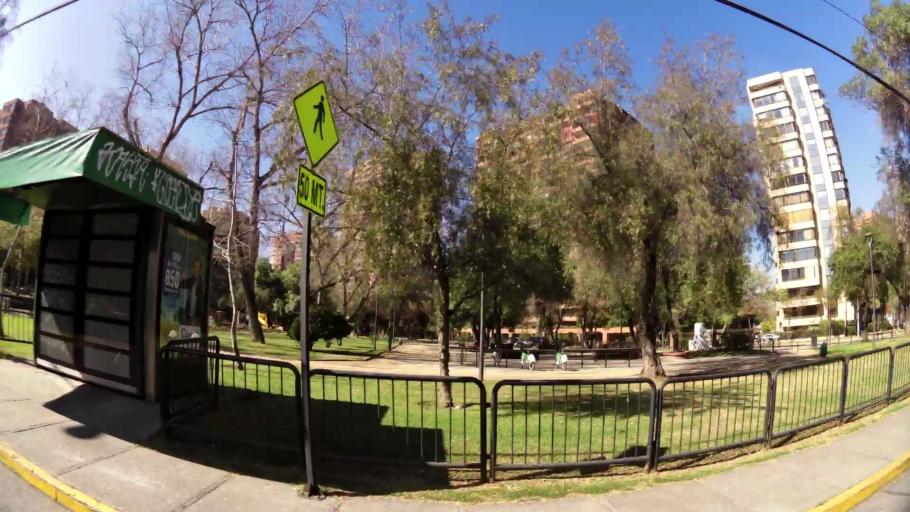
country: CL
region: Santiago Metropolitan
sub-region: Provincia de Santiago
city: Villa Presidente Frei, Nunoa, Santiago, Chile
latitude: -33.3970
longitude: -70.5675
